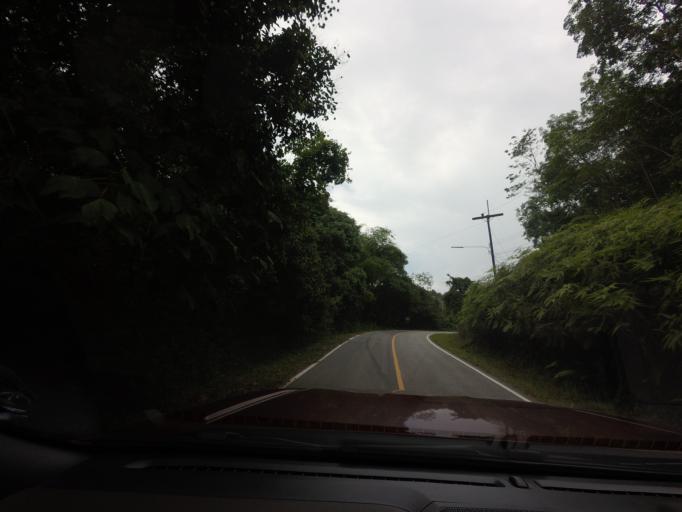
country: TH
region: Narathiwat
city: Sukhirin
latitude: 5.9845
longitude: 101.6817
